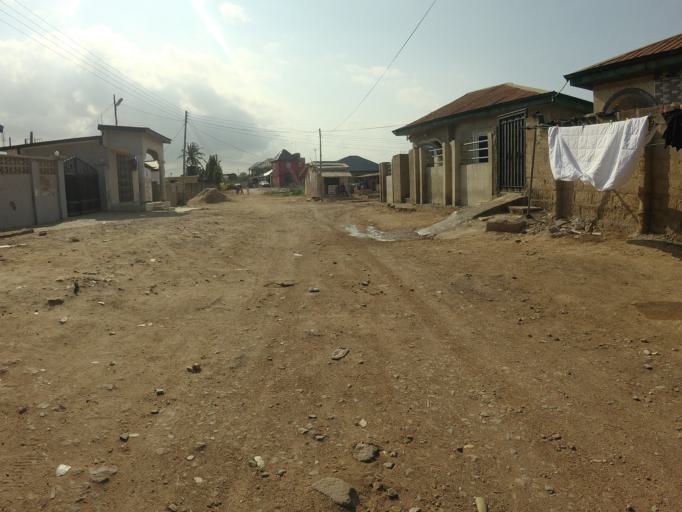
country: GH
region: Greater Accra
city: Dome
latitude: 5.6537
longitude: -0.2653
